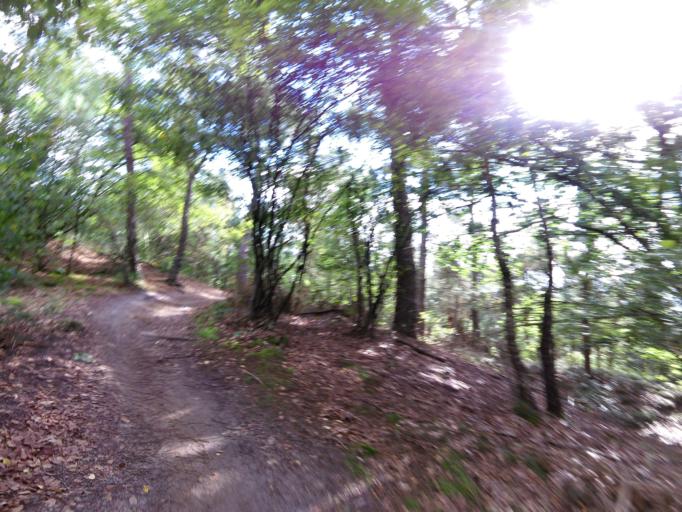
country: NL
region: North Brabant
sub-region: Gemeente Loon op Zand
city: Loon op Zand
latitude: 51.6364
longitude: 5.0974
